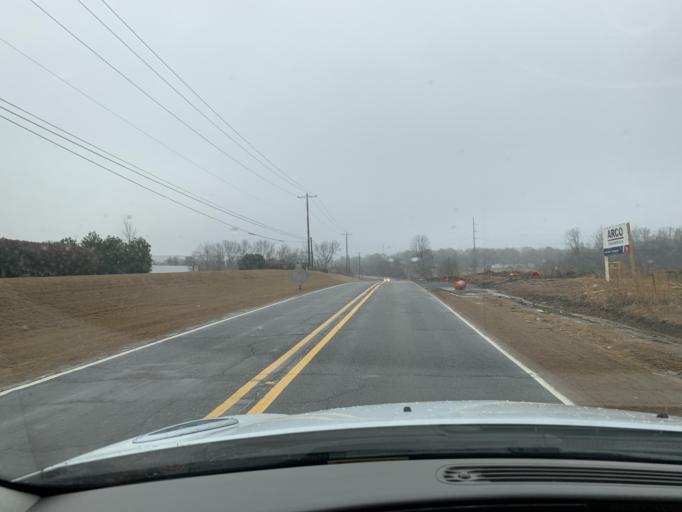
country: US
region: Mississippi
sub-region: De Soto County
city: Horn Lake
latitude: 34.9144
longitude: -90.0037
